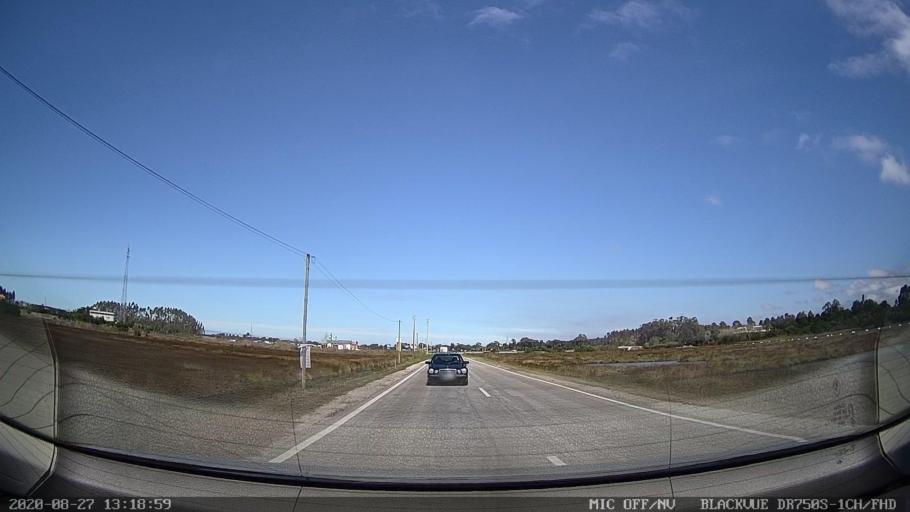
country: PT
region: Aveiro
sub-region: Vagos
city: Vagos
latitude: 40.5691
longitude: -8.6827
